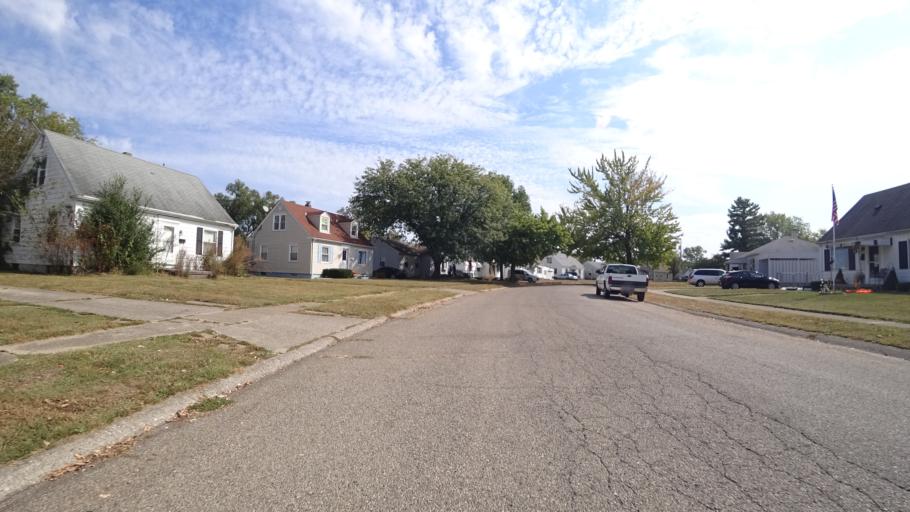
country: US
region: Ohio
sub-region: Butler County
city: Fairfield
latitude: 39.3605
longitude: -84.5451
